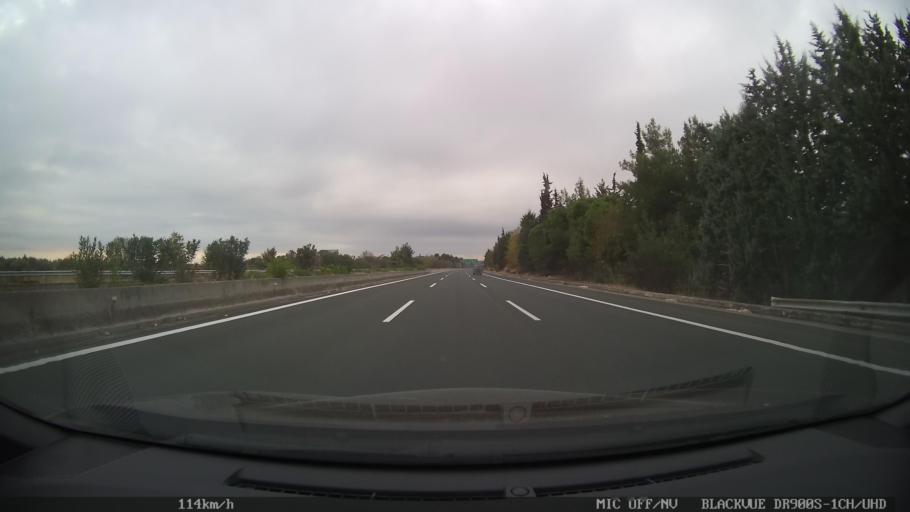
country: GR
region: Central Macedonia
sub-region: Nomos Pierias
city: Makrygialos
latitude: 40.4298
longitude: 22.5883
